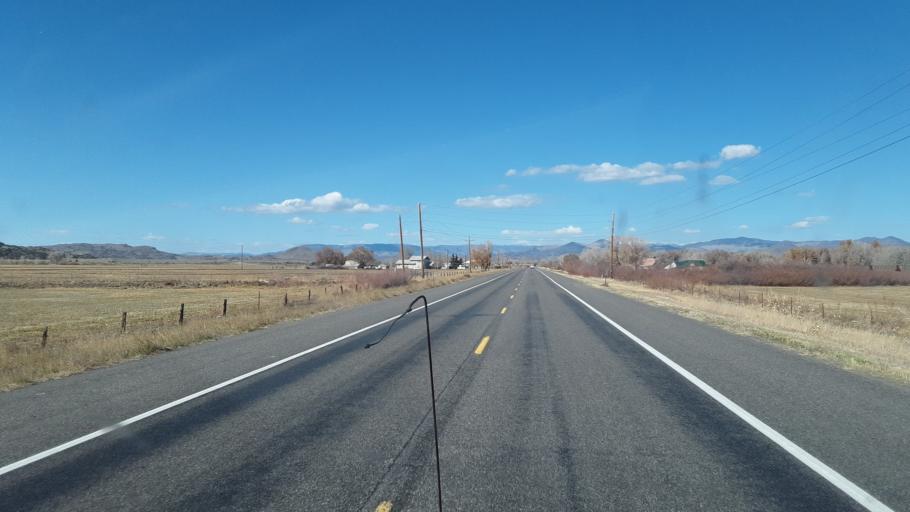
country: US
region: Colorado
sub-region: Rio Grande County
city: Del Norte
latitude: 37.6529
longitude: -106.2812
